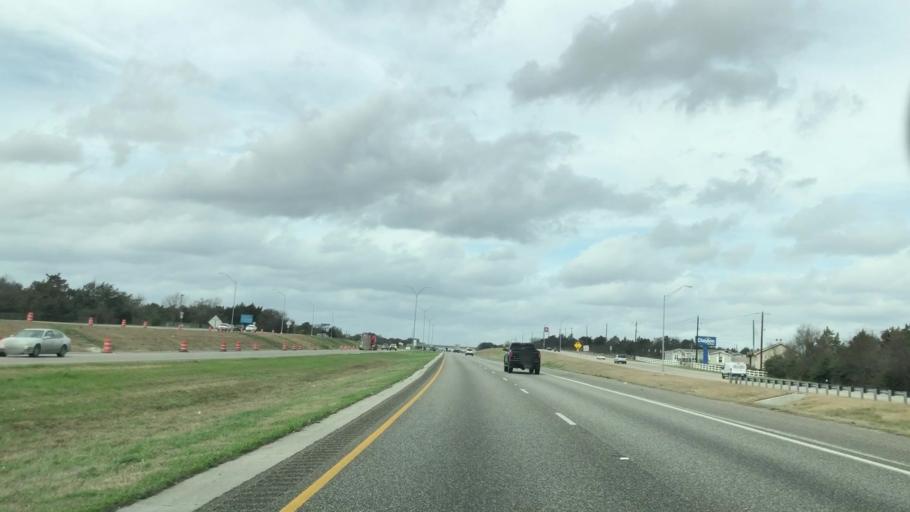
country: US
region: Texas
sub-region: Brazos County
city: Bryan
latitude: 30.6909
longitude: -96.3521
